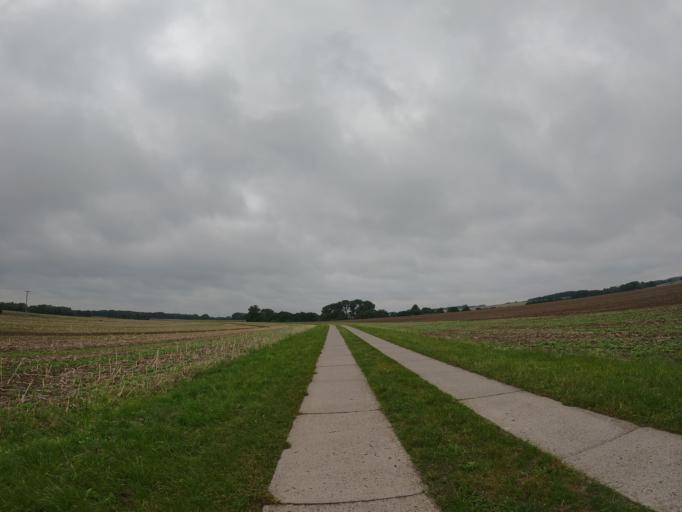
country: DE
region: Mecklenburg-Vorpommern
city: Poseritz
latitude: 54.2767
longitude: 13.2469
